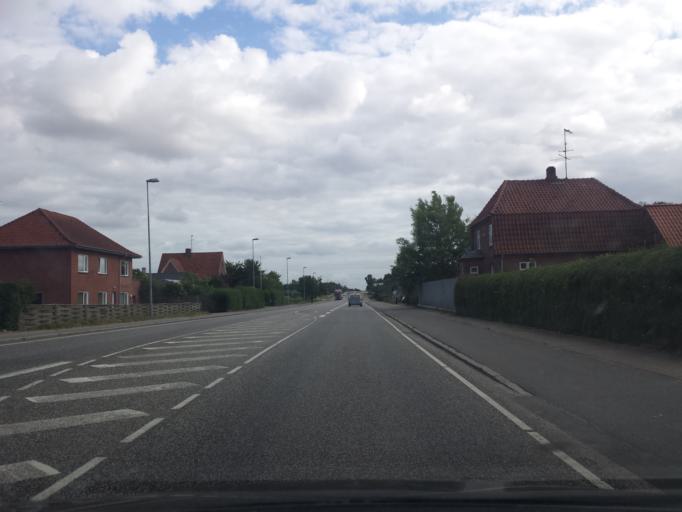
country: DK
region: South Denmark
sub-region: Sonderborg Kommune
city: Augustenborg
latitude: 54.9683
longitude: 9.8989
